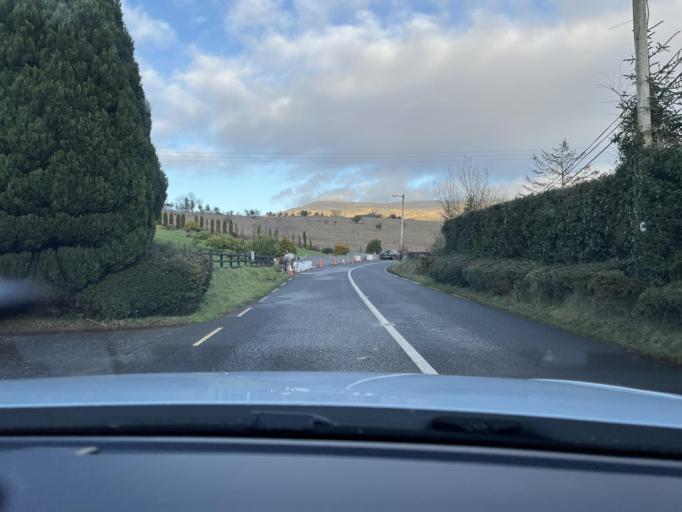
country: GB
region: Northern Ireland
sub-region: Fermanagh District
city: Enniskillen
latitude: 54.1912
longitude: -7.8962
